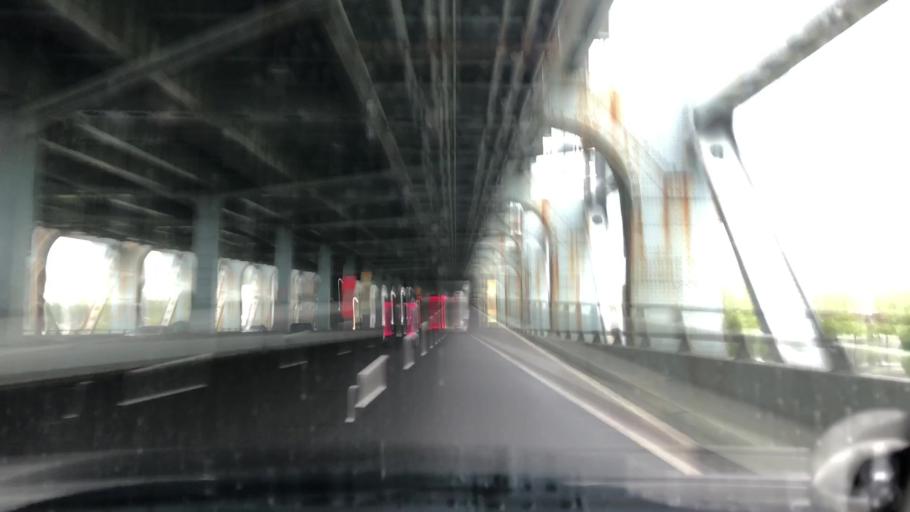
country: US
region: New York
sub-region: Kings County
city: Bensonhurst
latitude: 40.6035
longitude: -74.0552
